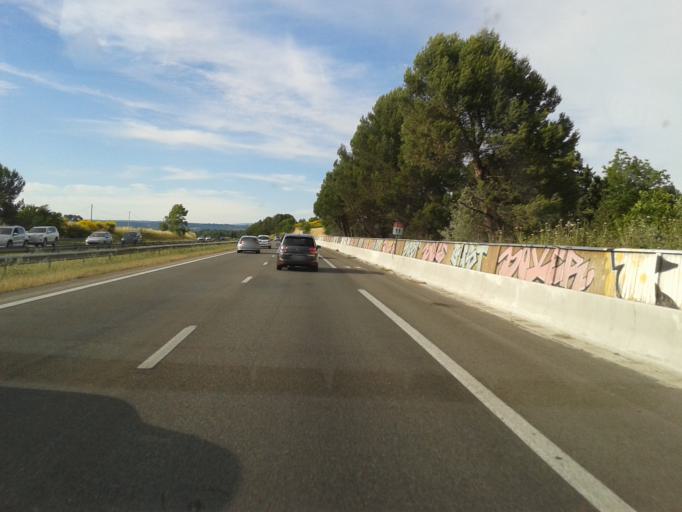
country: FR
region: Provence-Alpes-Cote d'Azur
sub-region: Departement des Bouches-du-Rhone
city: Bouc-Bel-Air
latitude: 43.4759
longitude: 5.4079
